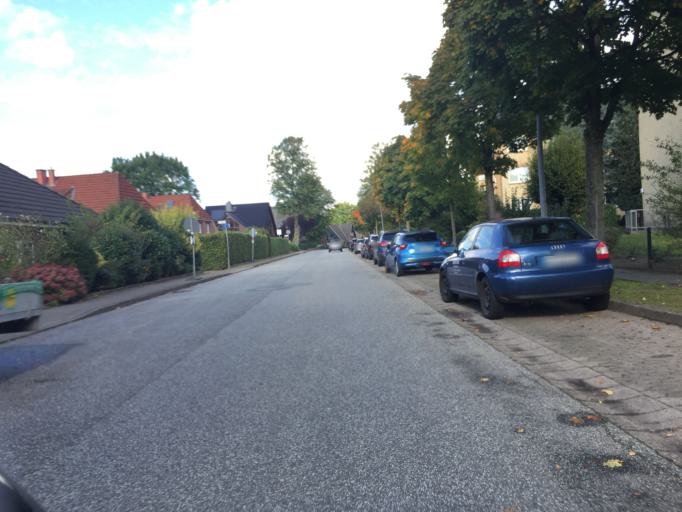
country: DE
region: Schleswig-Holstein
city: Heiligenstedten
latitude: 53.9421
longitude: 9.4942
